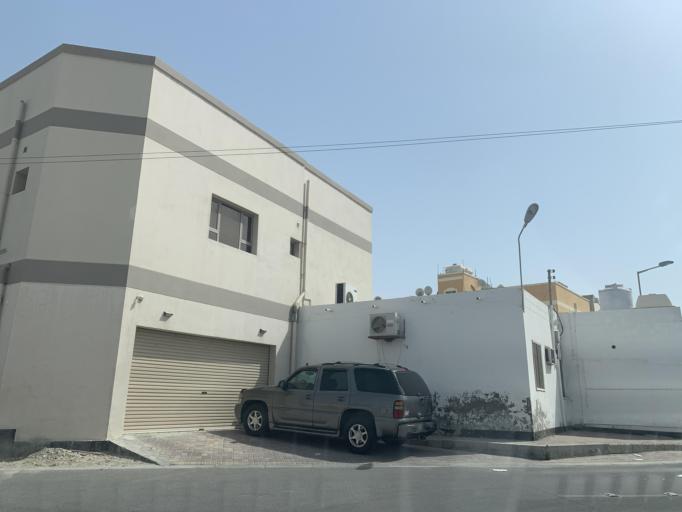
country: BH
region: Northern
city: Madinat `Isa
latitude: 26.1860
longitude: 50.5483
